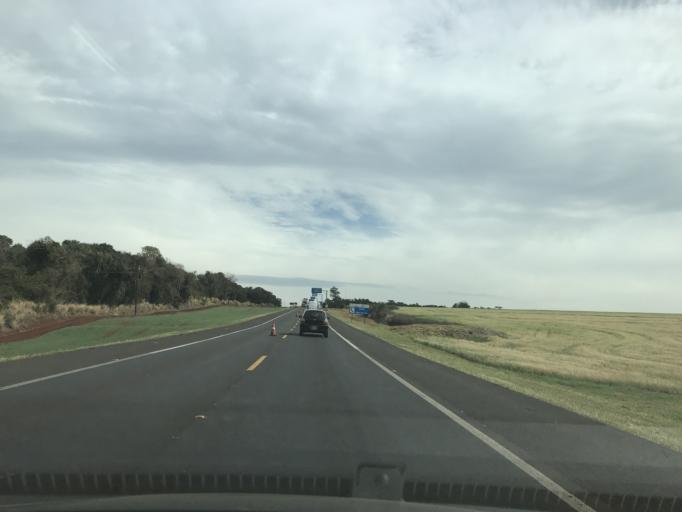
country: BR
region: Parana
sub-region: Cascavel
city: Cascavel
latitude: -25.0803
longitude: -53.7040
